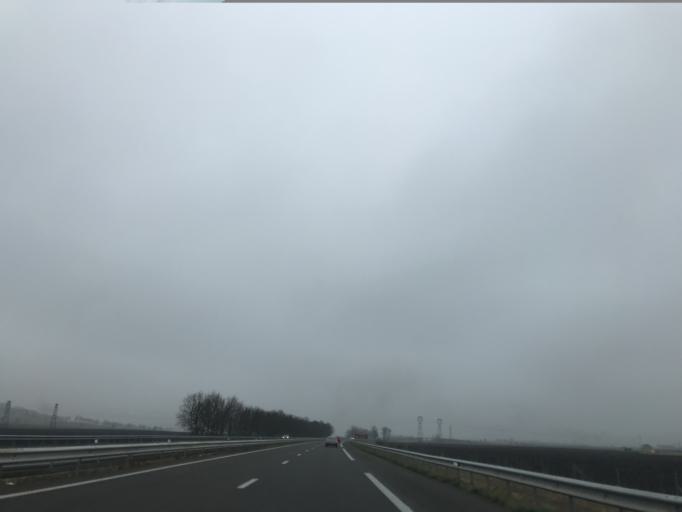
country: FR
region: Auvergne
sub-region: Departement du Puy-de-Dome
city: Pont-du-Chateau
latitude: 45.8153
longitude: 3.2230
